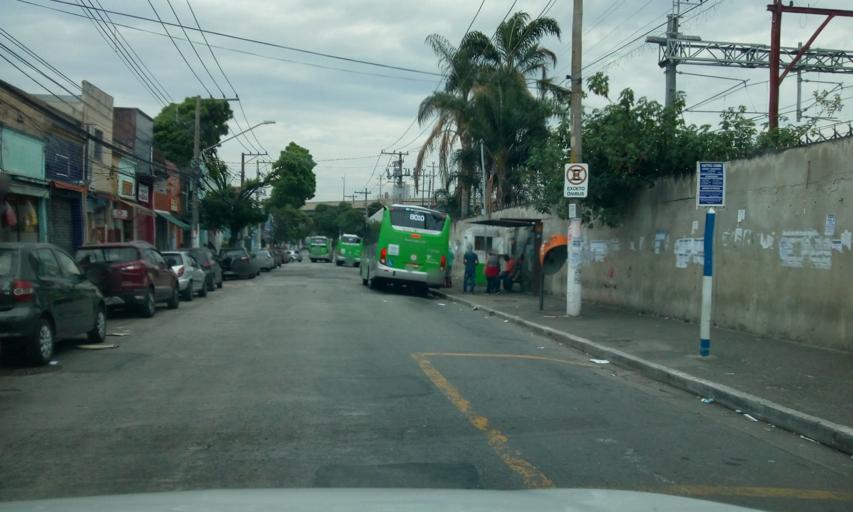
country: BR
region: Sao Paulo
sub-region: Sao Paulo
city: Sao Paulo
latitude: -23.5182
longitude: -46.7021
